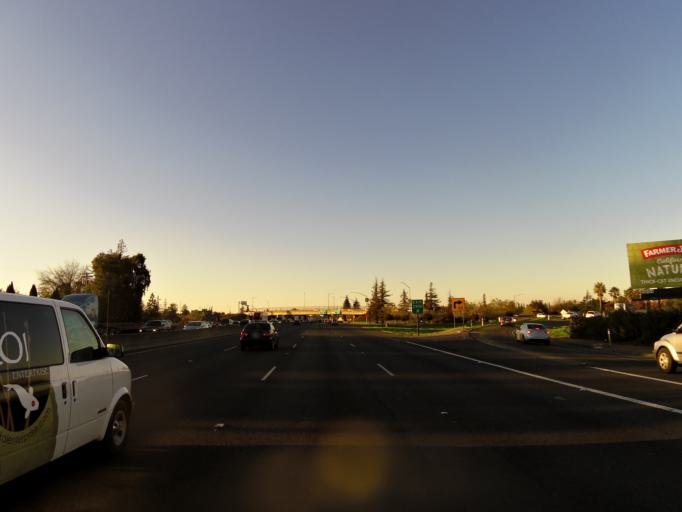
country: US
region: California
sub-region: Sacramento County
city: Parkway
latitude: 38.4941
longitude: -121.4437
